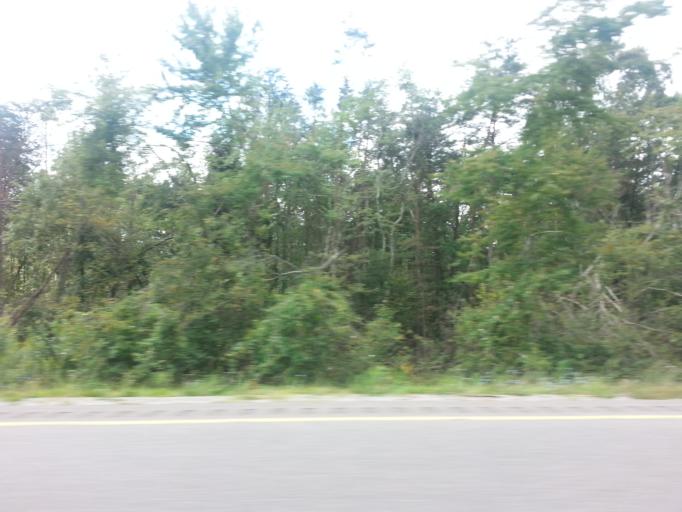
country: US
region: Tennessee
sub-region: Cumberland County
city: Crossville
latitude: 36.0342
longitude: -85.0979
